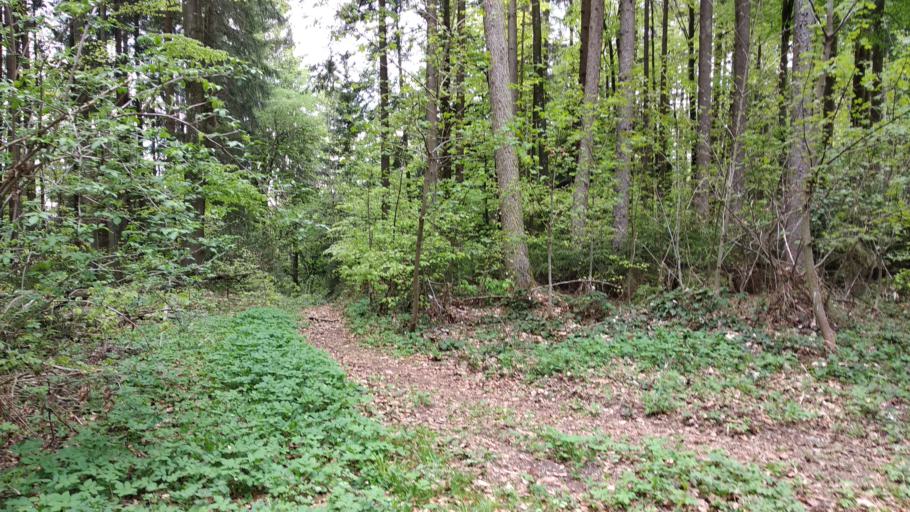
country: DE
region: Bavaria
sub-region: Swabia
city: Woringen
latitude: 47.9266
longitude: 10.1895
